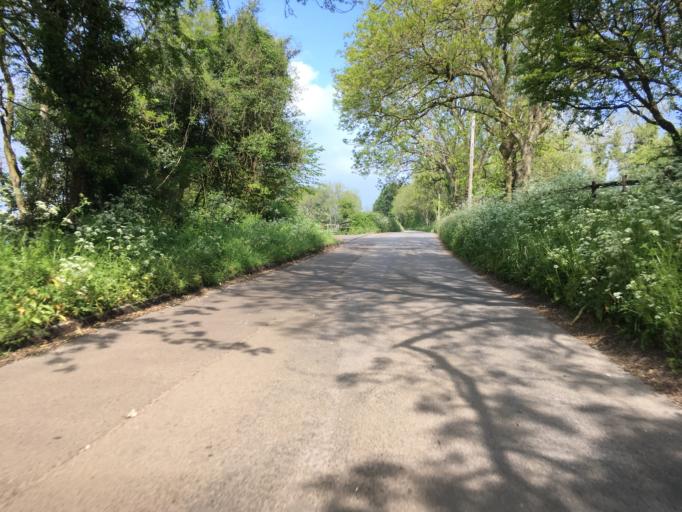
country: GB
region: England
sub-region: North Somerset
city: Butcombe
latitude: 51.3948
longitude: -2.7118
